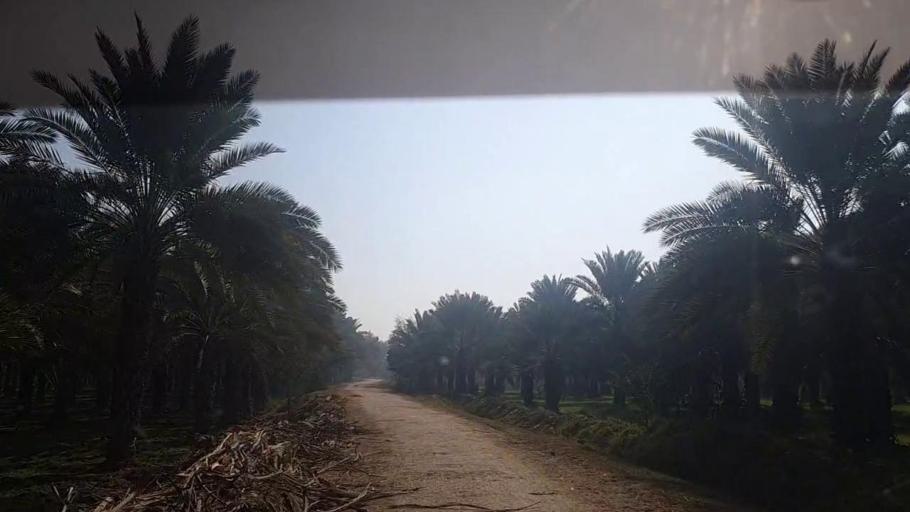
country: PK
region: Sindh
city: Khairpur
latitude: 27.4752
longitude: 68.7258
